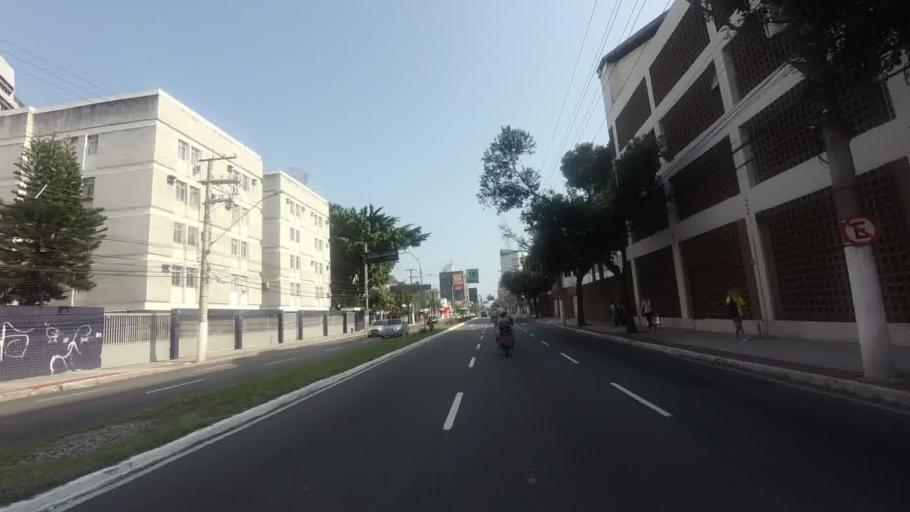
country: BR
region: Espirito Santo
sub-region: Vila Velha
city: Vila Velha
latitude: -20.3040
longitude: -40.2975
